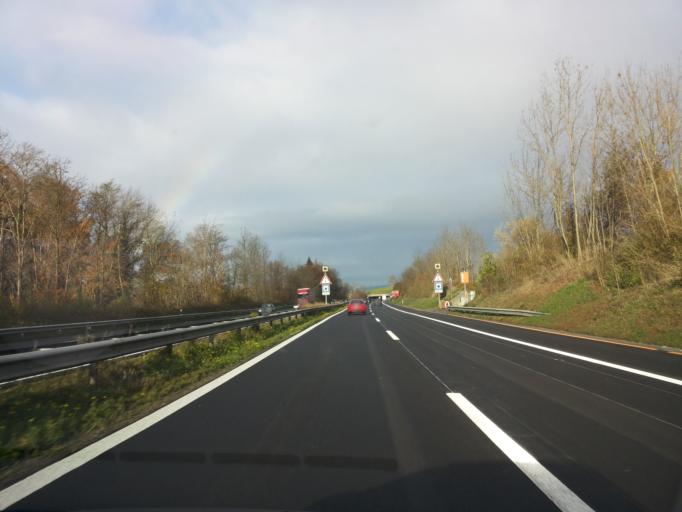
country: CH
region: Lucerne
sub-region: Sursee District
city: Schenkon
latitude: 47.1720
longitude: 8.1338
